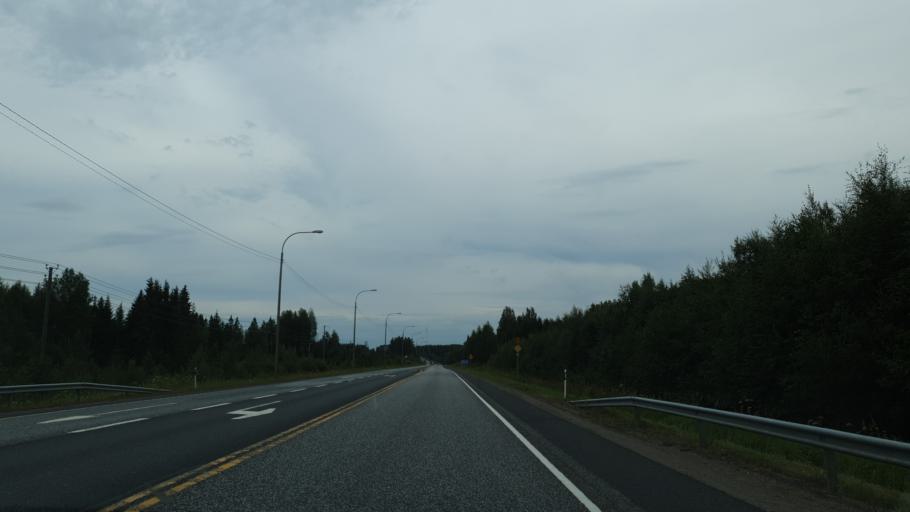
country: FI
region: North Karelia
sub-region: Joensuu
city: Pyhaeselkae
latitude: 62.5140
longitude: 29.8925
